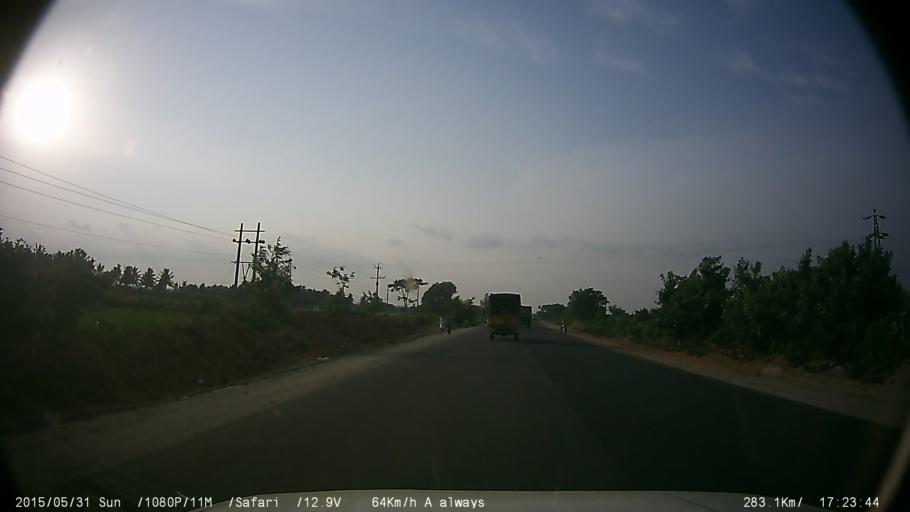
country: IN
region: Karnataka
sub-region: Chamrajnagar
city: Gundlupet
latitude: 11.8427
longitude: 76.6732
